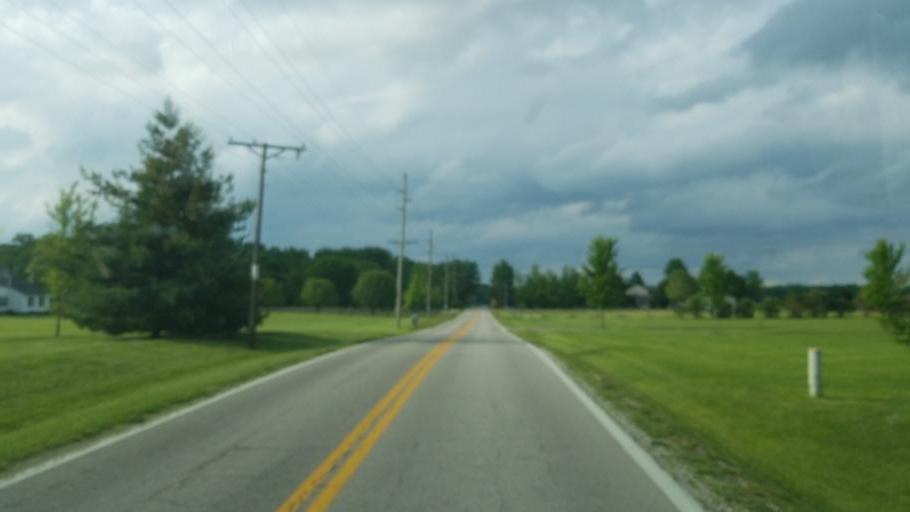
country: US
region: Ohio
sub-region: Knox County
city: Centerburg
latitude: 40.3065
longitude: -82.7843
